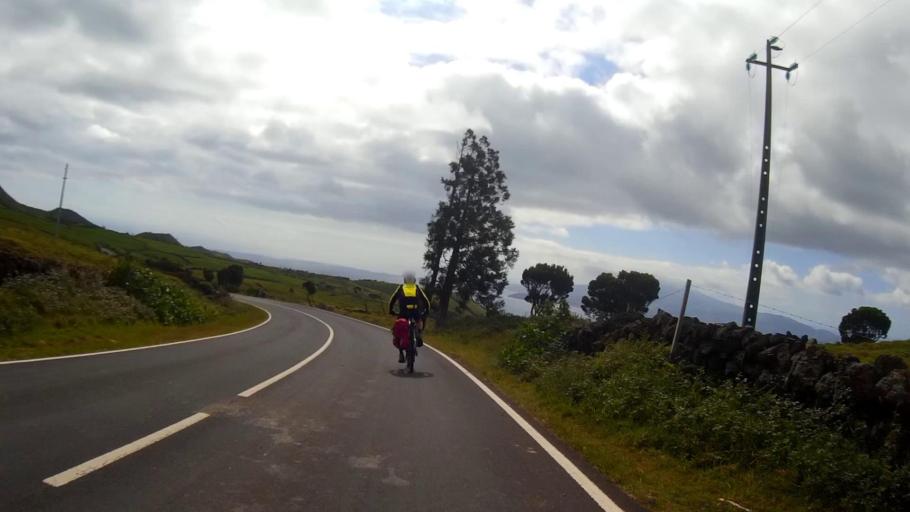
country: PT
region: Azores
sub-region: Madalena
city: Madalena
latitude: 38.4972
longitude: -28.4505
